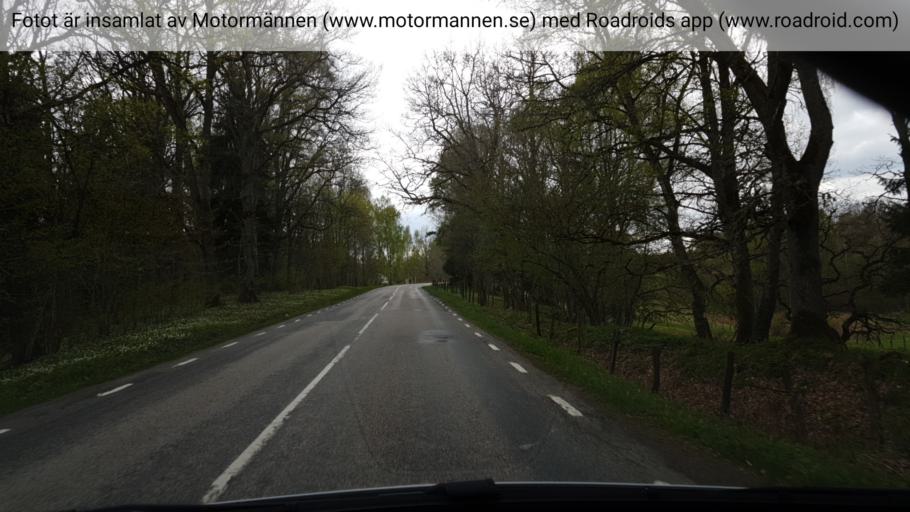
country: SE
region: Vaestra Goetaland
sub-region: Falkopings Kommun
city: Floby
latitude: 58.1114
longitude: 13.2829
